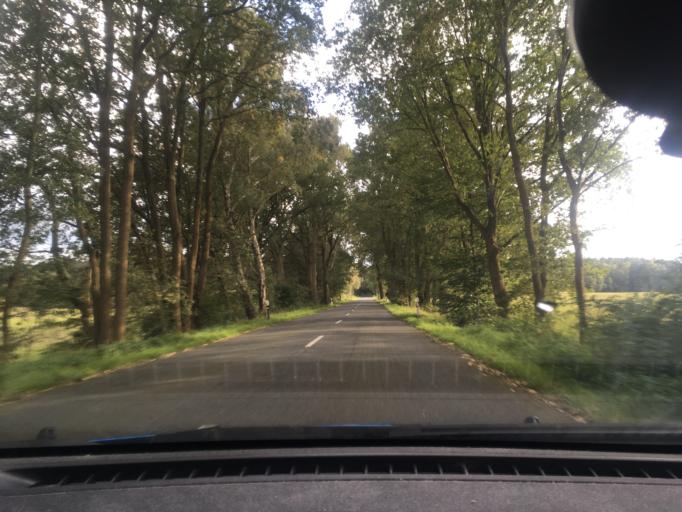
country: DE
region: Lower Saxony
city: Gohrde
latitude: 53.1593
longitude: 10.8667
